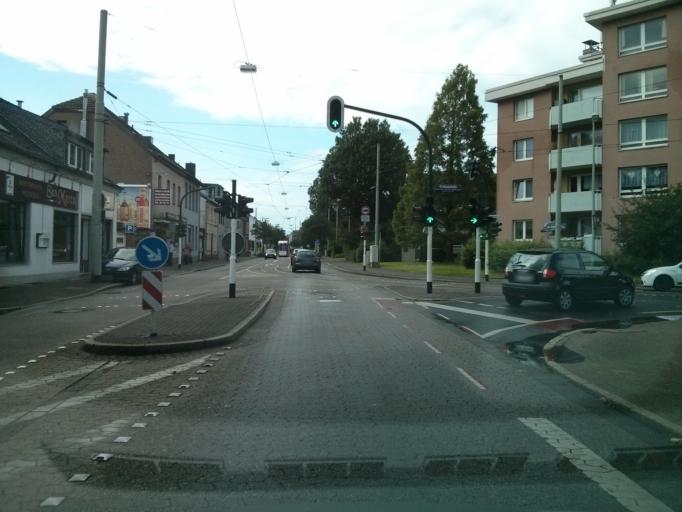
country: DE
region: North Rhine-Westphalia
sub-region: Regierungsbezirk Dusseldorf
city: Krefeld
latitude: 51.3004
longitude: 6.5922
